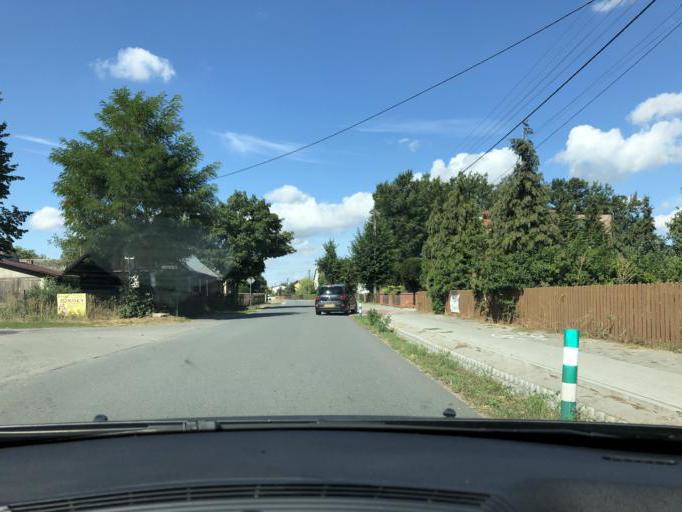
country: PL
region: Lodz Voivodeship
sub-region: Powiat wieruszowski
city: Czastary
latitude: 51.2402
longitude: 18.3335
